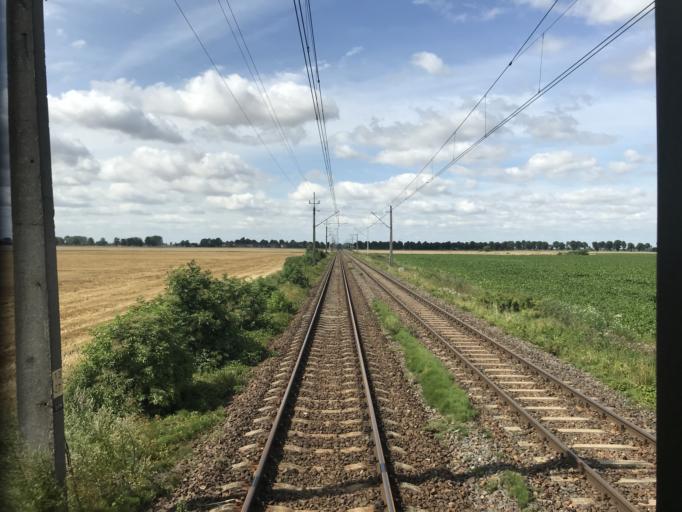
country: PL
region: Pomeranian Voivodeship
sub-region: Powiat malborski
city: Stare Pole
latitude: 54.0654
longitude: 19.2434
